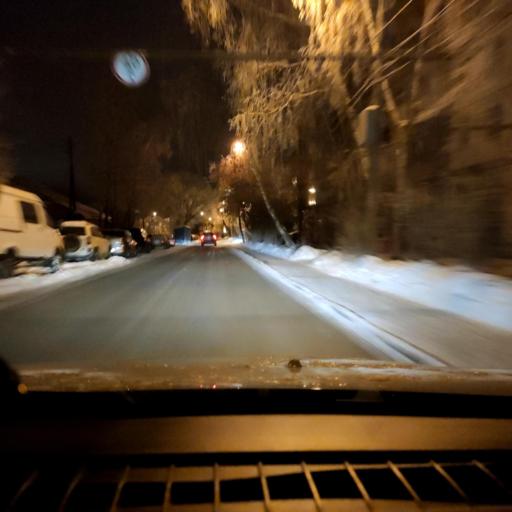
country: RU
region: Samara
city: Novosemeykino
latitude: 53.3462
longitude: 50.2281
